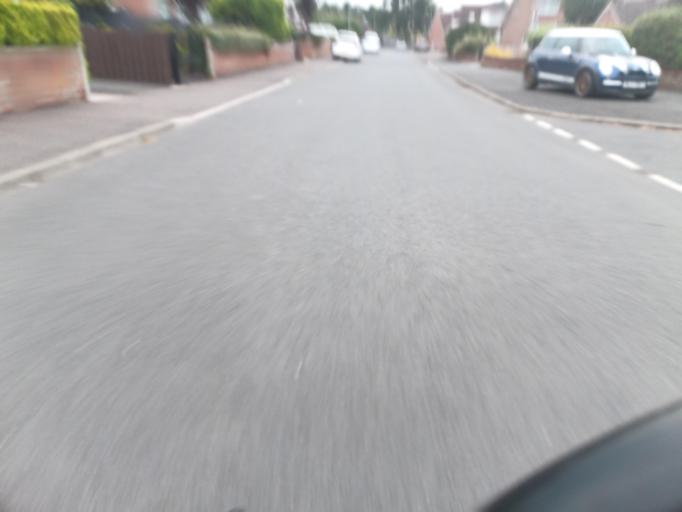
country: GB
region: Northern Ireland
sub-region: Ards District
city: Comber
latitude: 54.5538
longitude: -5.7303
